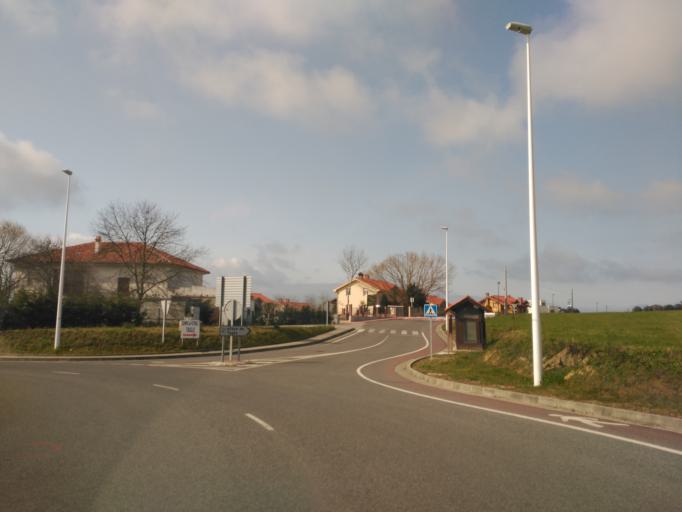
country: ES
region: Cantabria
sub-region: Provincia de Cantabria
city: Suances
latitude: 43.4209
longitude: -4.0685
